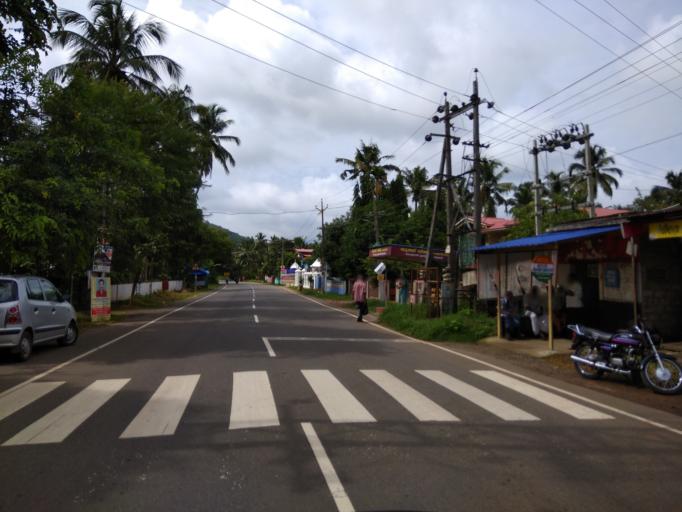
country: IN
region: Kerala
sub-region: Thrissur District
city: Trichur
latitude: 10.5394
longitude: 76.3325
